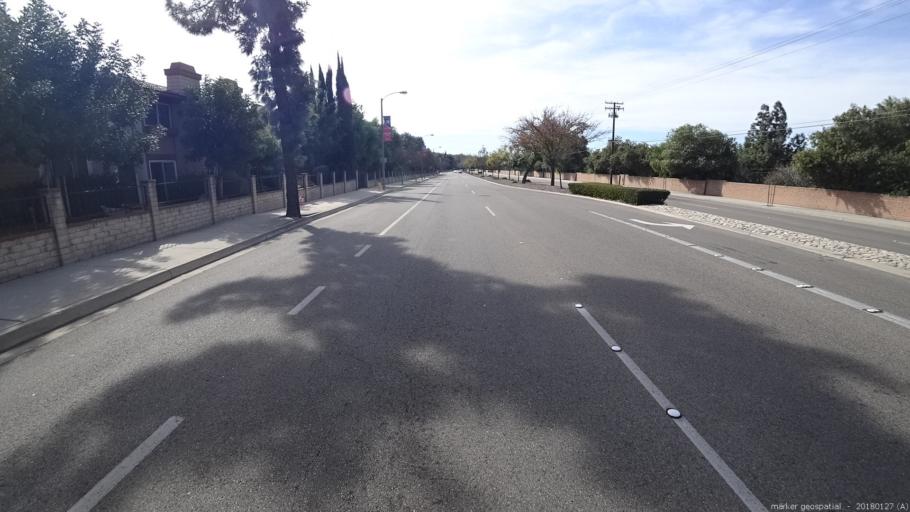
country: US
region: California
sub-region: Los Angeles County
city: Diamond Bar
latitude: 33.9810
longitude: -117.8310
